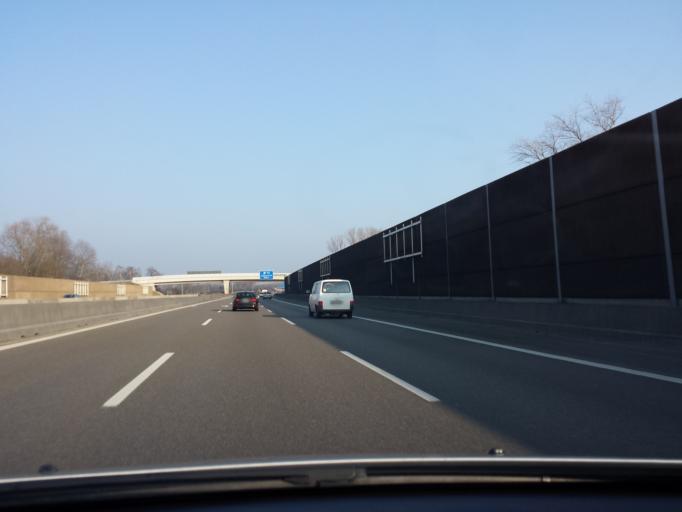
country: DE
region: Bavaria
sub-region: Swabia
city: Gersthofen
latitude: 48.4139
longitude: 10.8916
